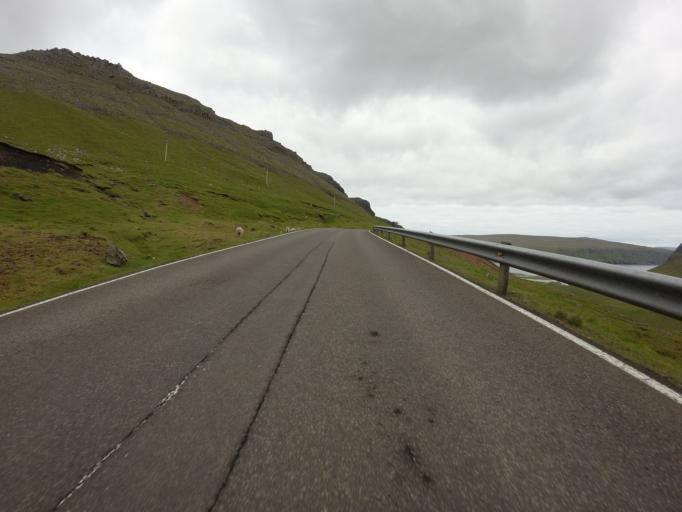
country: FO
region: Suduroy
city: Tvoroyri
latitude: 61.5740
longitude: -6.9362
